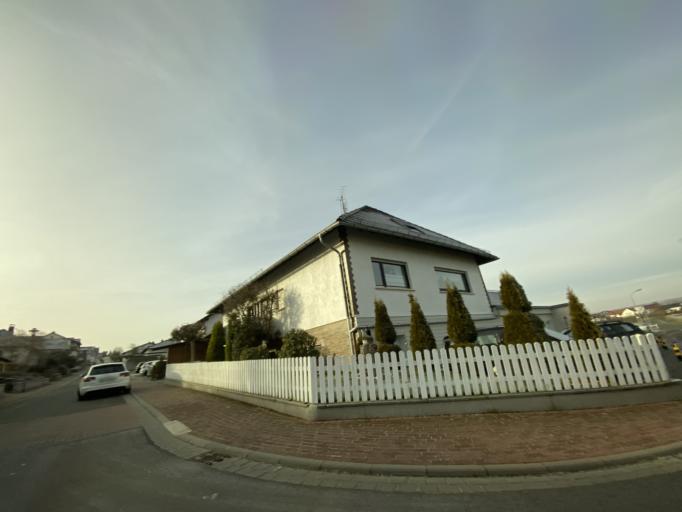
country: DE
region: Hesse
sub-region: Regierungsbezirk Giessen
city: Ebsdorfergrund
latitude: 50.7602
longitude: 8.8876
